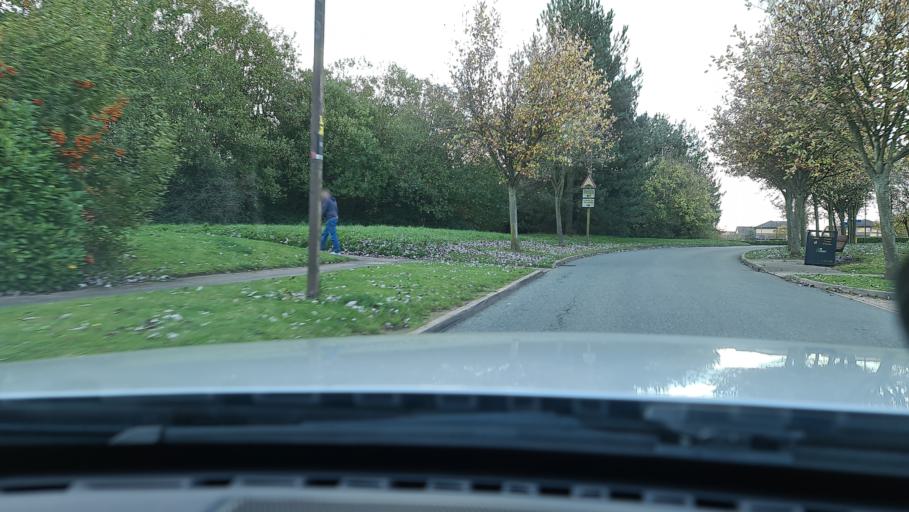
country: GB
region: England
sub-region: Milton Keynes
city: Simpson
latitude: 52.0223
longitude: -0.6929
